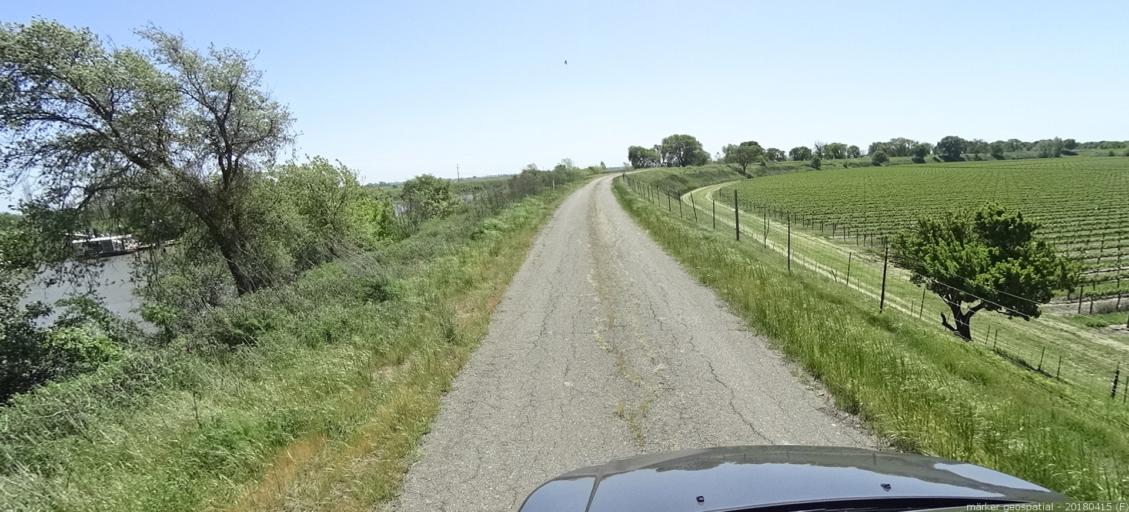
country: US
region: California
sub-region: Sacramento County
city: Walnut Grove
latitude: 38.2593
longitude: -121.5952
